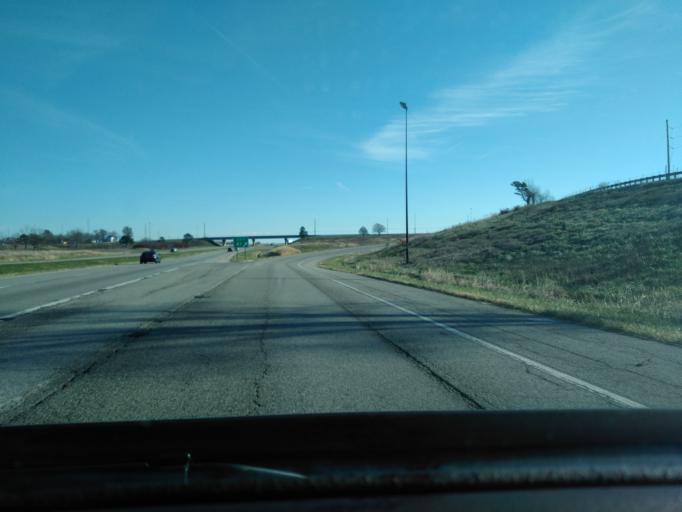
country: US
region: Illinois
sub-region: Bond County
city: Greenville
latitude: 38.8521
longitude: -89.4563
